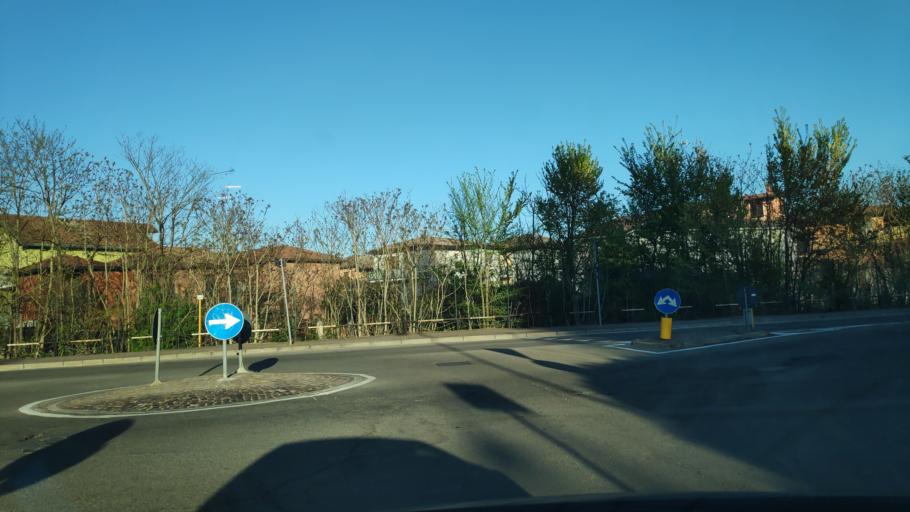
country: IT
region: Lombardy
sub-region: Citta metropolitana di Milano
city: Pieve Emanuele
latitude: 45.3539
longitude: 9.2013
